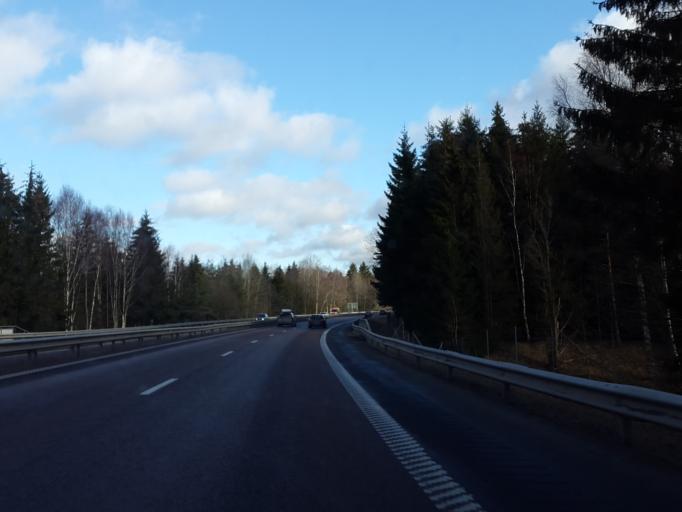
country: SE
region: Vaestra Goetaland
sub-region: Lerums Kommun
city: Lerum
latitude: 57.7459
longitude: 12.2249
